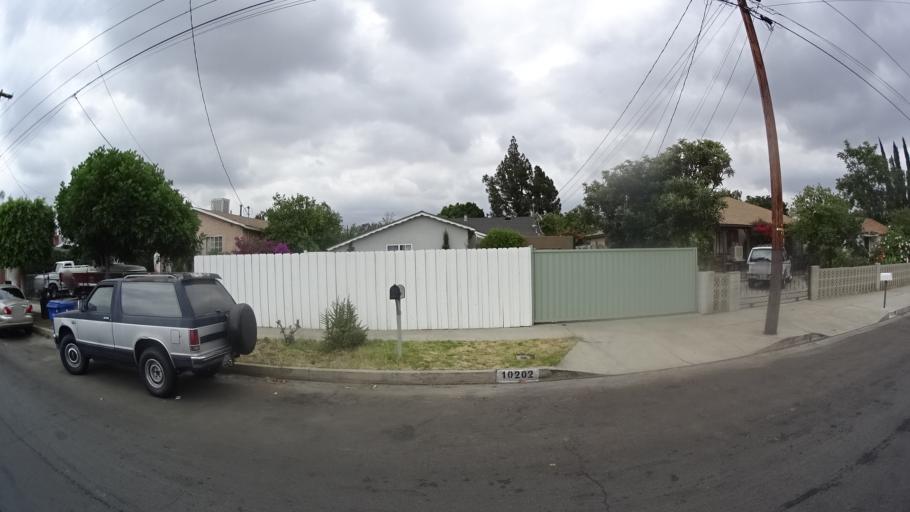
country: US
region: California
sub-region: Los Angeles County
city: San Fernando
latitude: 34.2556
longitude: -118.4390
